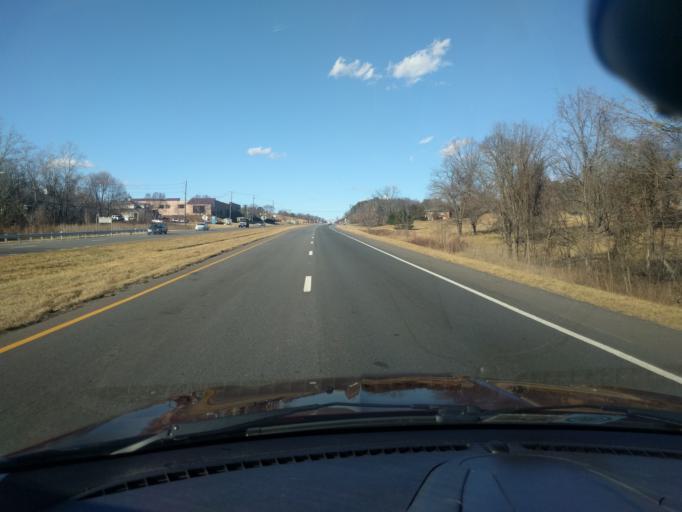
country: US
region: Virginia
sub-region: Botetourt County
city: Cloverdale
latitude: 37.3538
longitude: -79.8842
